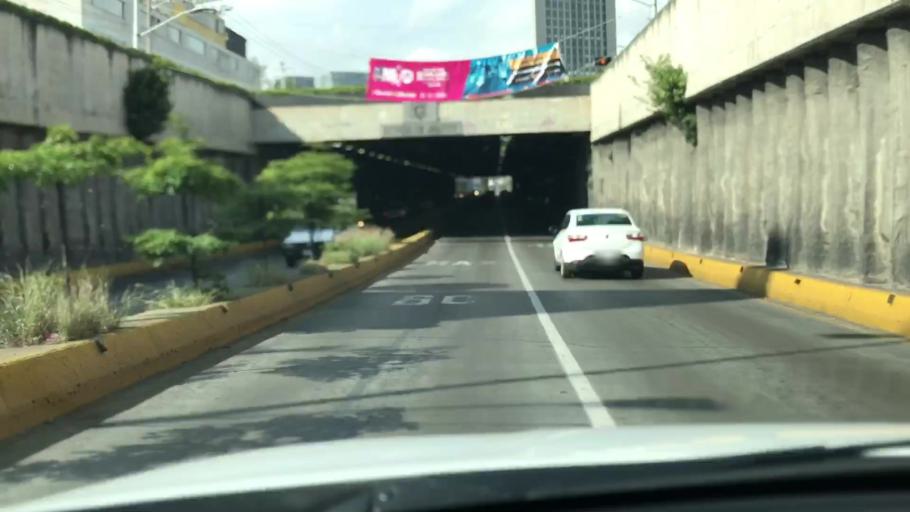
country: MX
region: Jalisco
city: Guadalajara
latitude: 20.6857
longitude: -103.3800
